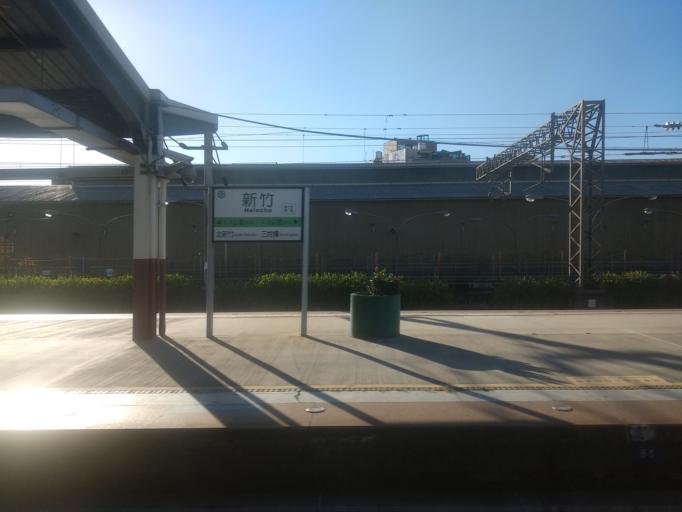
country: TW
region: Taiwan
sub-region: Hsinchu
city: Hsinchu
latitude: 24.8008
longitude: 120.9711
